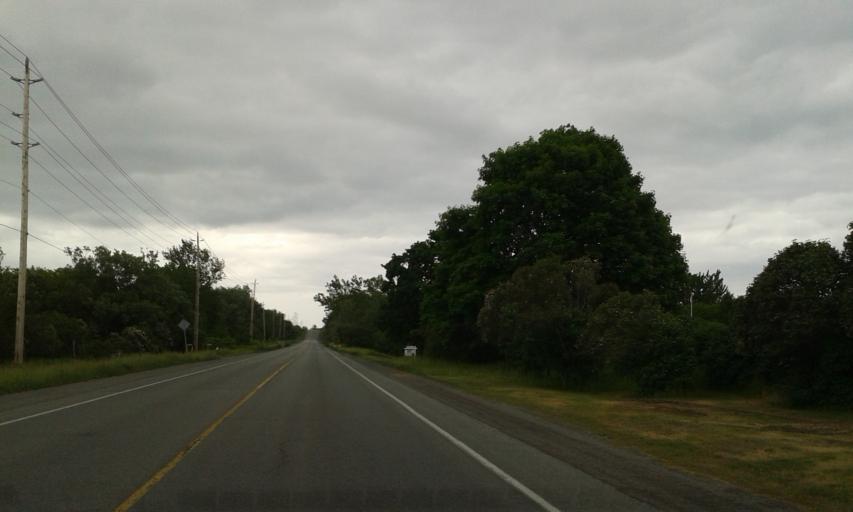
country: CA
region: Ontario
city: Quinte West
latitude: 43.9980
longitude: -77.5187
